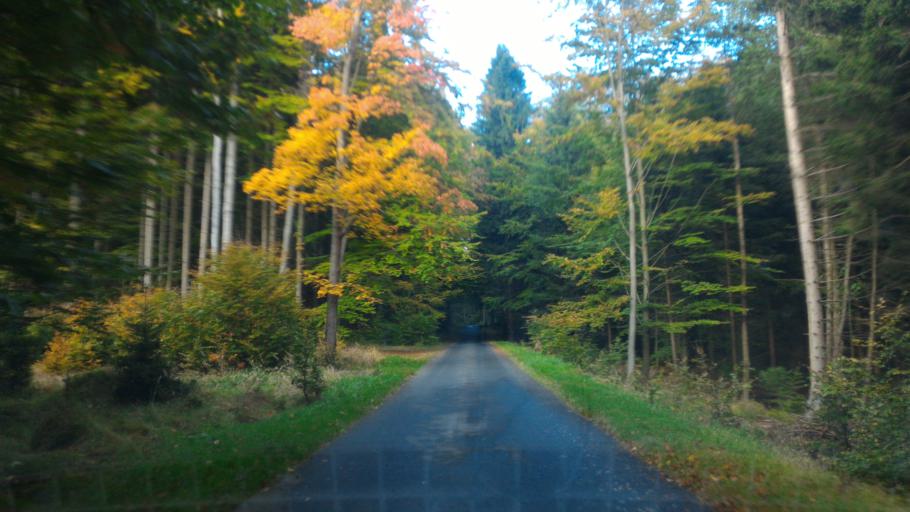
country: CZ
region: Ustecky
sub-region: Okres Decin
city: Chribska
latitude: 50.8240
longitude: 14.4886
